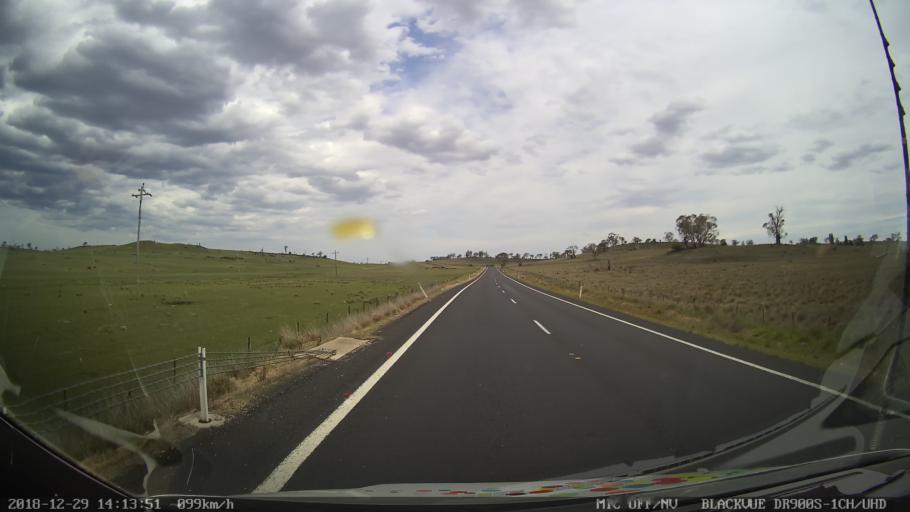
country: AU
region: New South Wales
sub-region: Cooma-Monaro
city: Cooma
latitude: -36.4341
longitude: 149.2382
